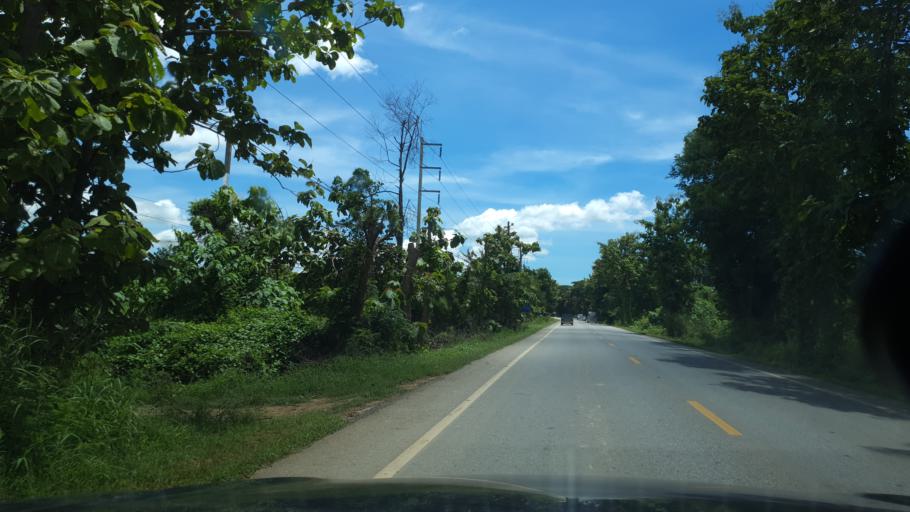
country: TH
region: Sukhothai
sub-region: Amphoe Si Satchanalai
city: Si Satchanalai
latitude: 17.4544
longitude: 99.7875
